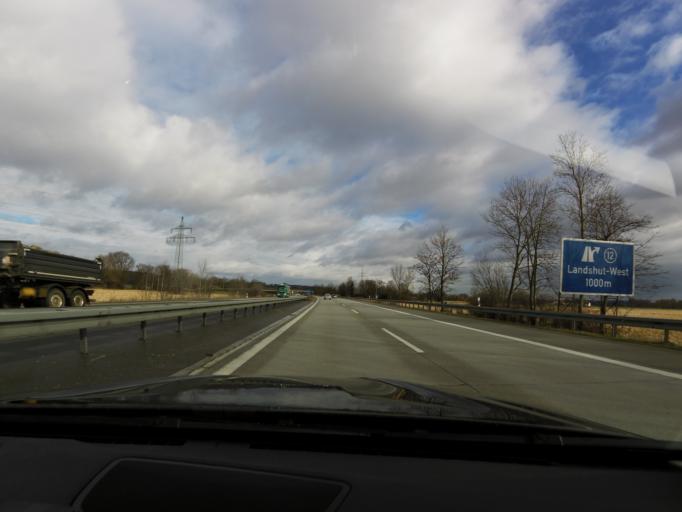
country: DE
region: Bavaria
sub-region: Lower Bavaria
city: Eching
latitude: 48.5211
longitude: 12.0652
